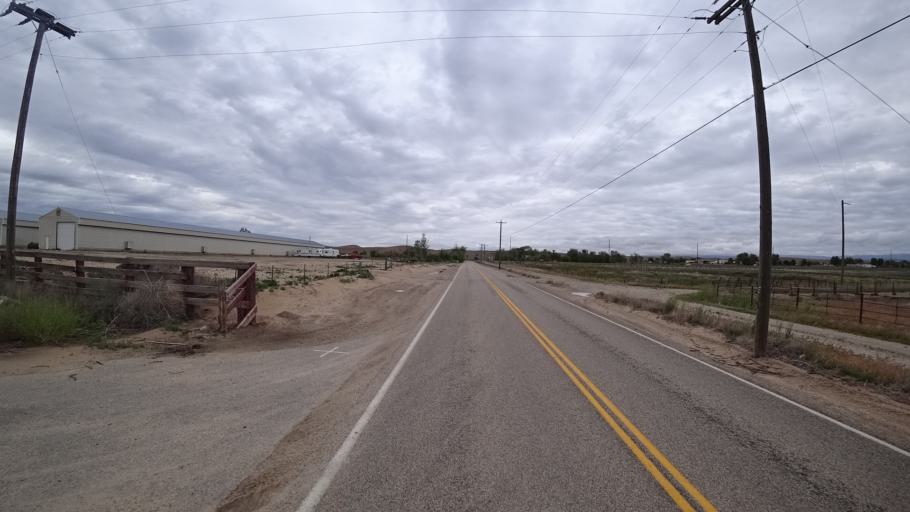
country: US
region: Idaho
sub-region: Ada County
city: Star
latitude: 43.7183
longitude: -116.4434
